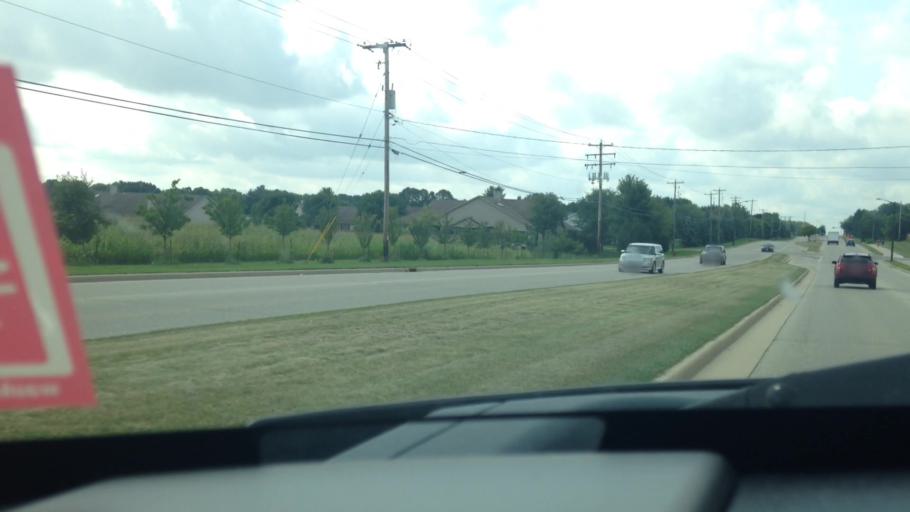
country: US
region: Wisconsin
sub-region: Waukesha County
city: Menomonee Falls
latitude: 43.1394
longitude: -88.1047
